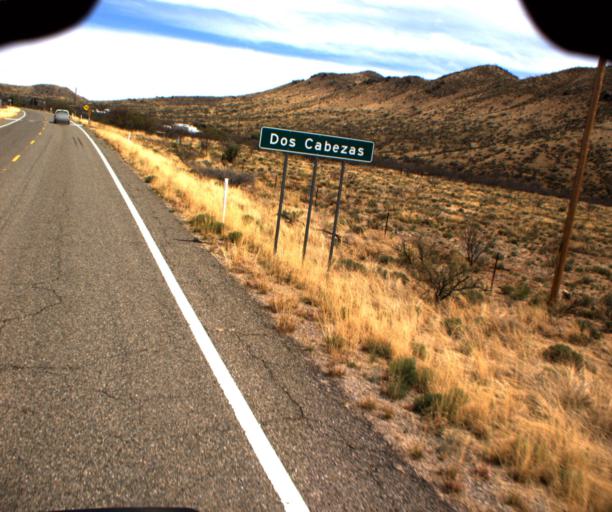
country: US
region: Arizona
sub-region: Cochise County
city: Willcox
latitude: 32.1759
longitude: -109.6207
